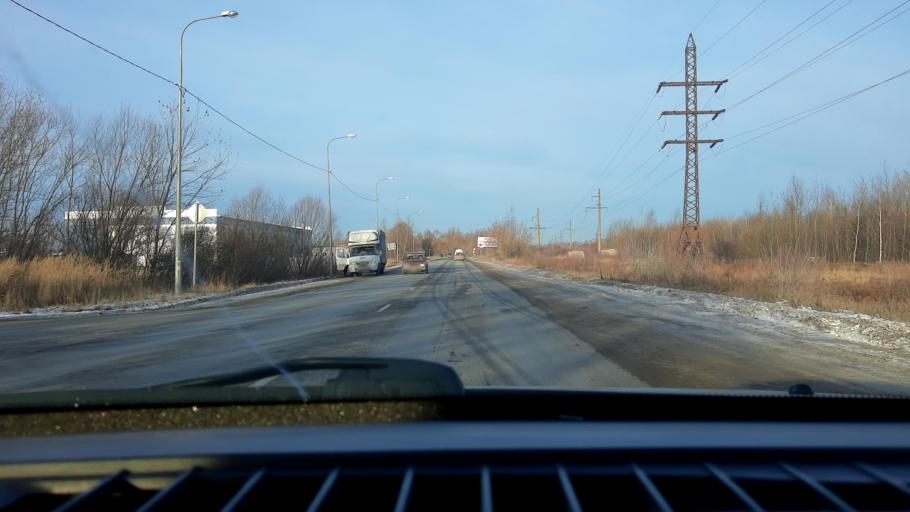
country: RU
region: Nizjnij Novgorod
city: Bor
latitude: 56.3740
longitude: 44.0624
